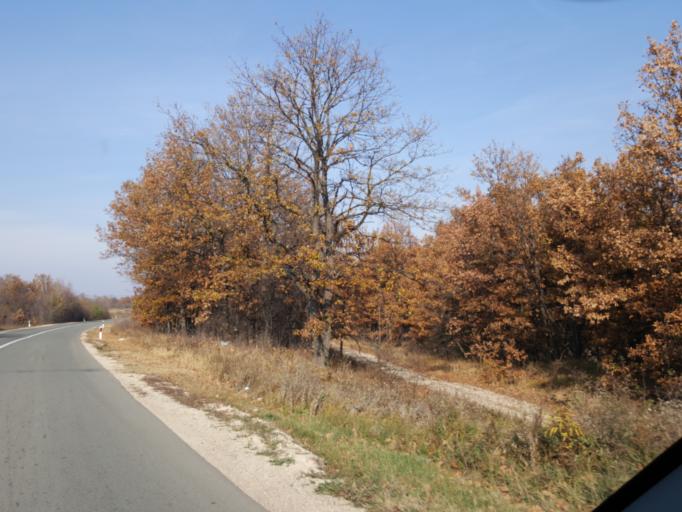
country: RS
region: Central Serbia
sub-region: Borski Okrug
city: Bor
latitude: 43.9998
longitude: 22.0707
